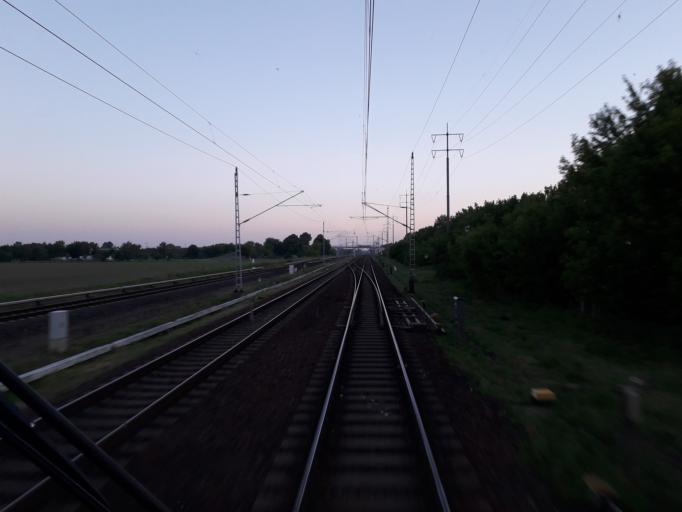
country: DE
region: Berlin
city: Blankenburg
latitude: 52.6135
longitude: 13.4509
